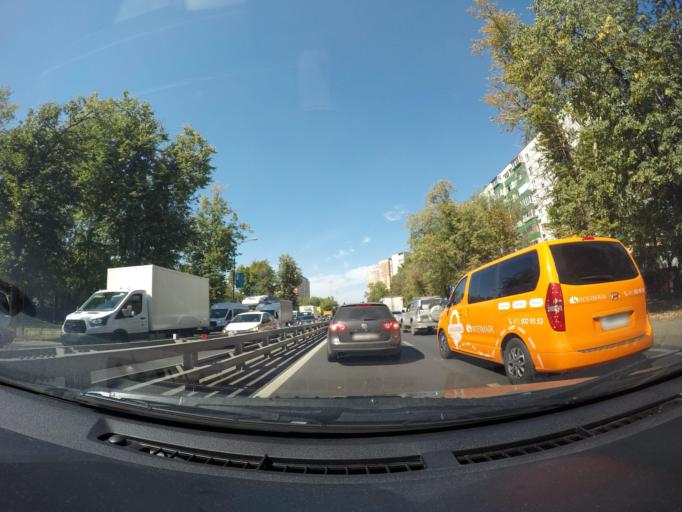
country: RU
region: Moscow
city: Zhulebino
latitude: 55.6953
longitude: 37.8623
